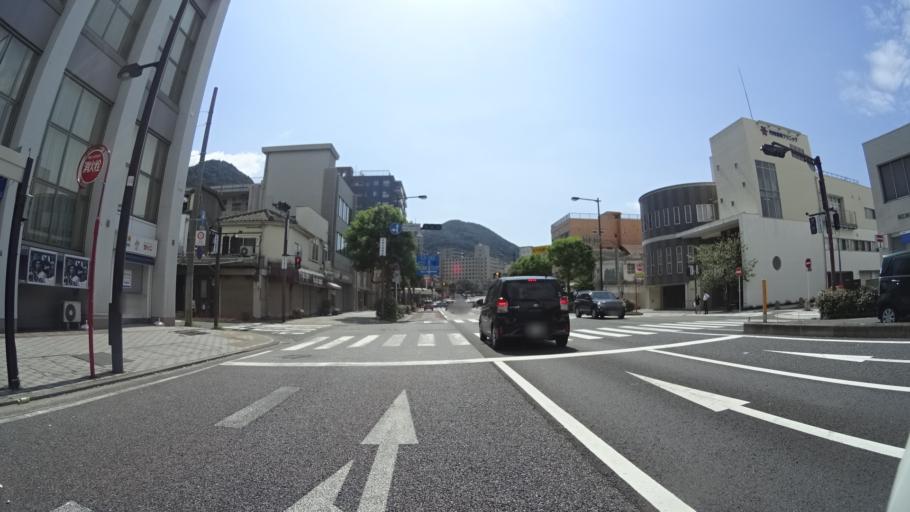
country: JP
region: Yamaguchi
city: Shimonoseki
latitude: 33.9452
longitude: 130.9647
